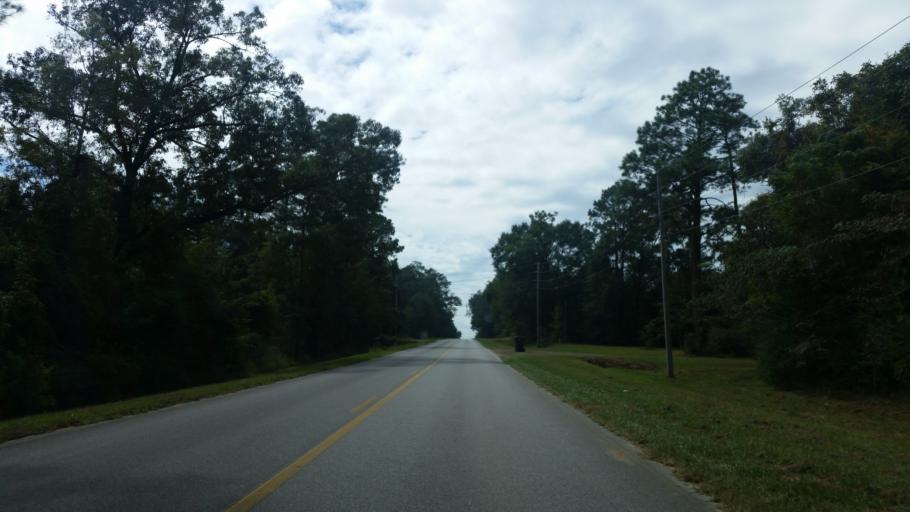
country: US
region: Florida
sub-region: Santa Rosa County
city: Point Baker
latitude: 30.8443
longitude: -86.8873
